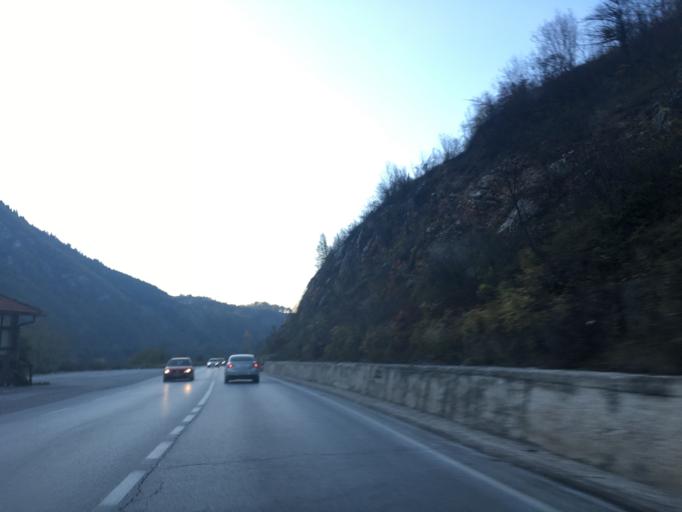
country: BA
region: Federation of Bosnia and Herzegovina
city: Kobilja Glava
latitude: 43.8438
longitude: 18.4769
